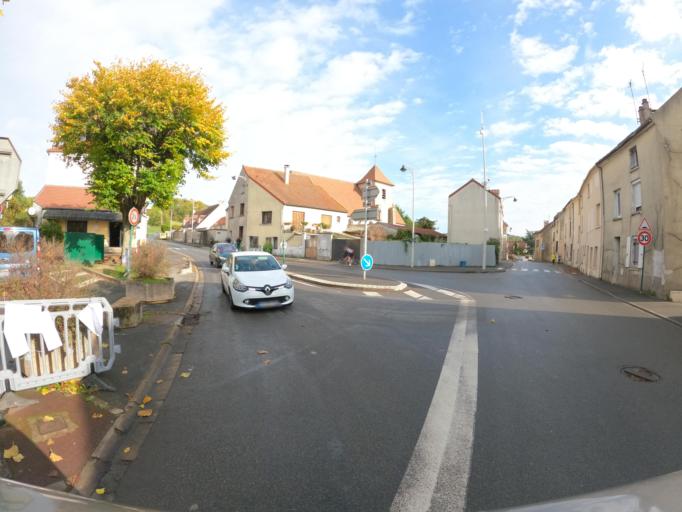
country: FR
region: Ile-de-France
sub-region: Departement de Seine-et-Marne
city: Courtry
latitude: 48.9182
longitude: 2.6034
